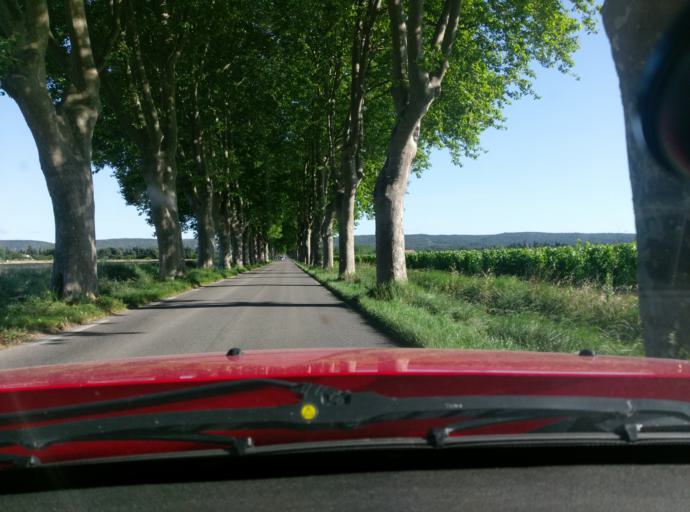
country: FR
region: Languedoc-Roussillon
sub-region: Departement du Gard
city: Uzes
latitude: 44.0359
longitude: 4.4091
